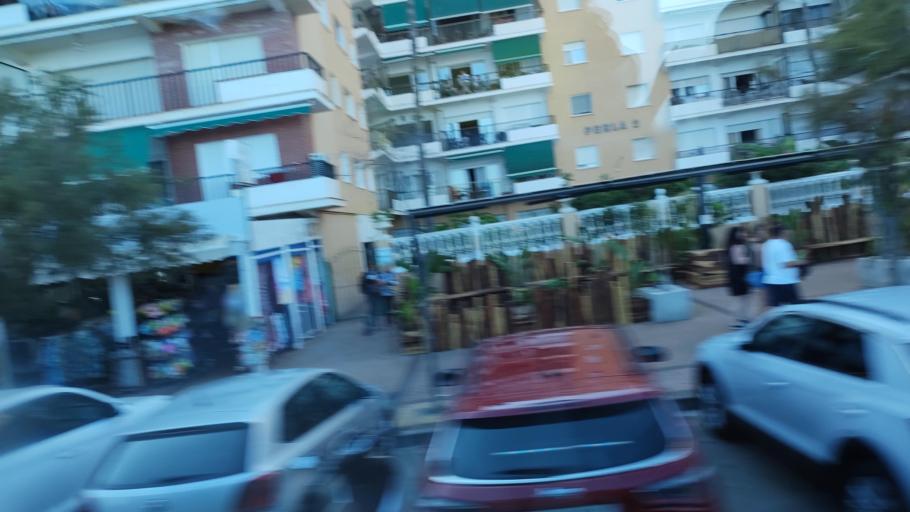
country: ES
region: Andalusia
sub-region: Provincia de Malaga
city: Fuengirola
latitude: 36.5377
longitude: -4.6216
